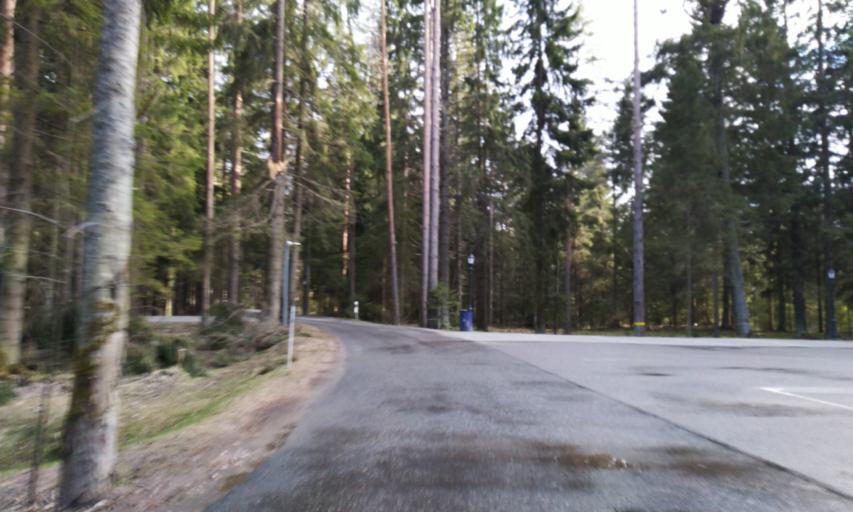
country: RU
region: Leningrad
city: Toksovo
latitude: 60.1304
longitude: 30.4521
